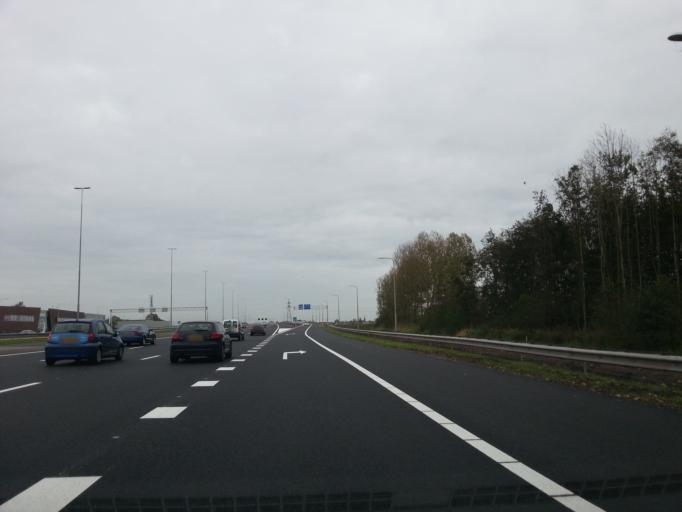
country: NL
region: South Holland
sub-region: Gemeente Leiderdorp
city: Leiderdorp
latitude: 52.1558
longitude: 4.5449
